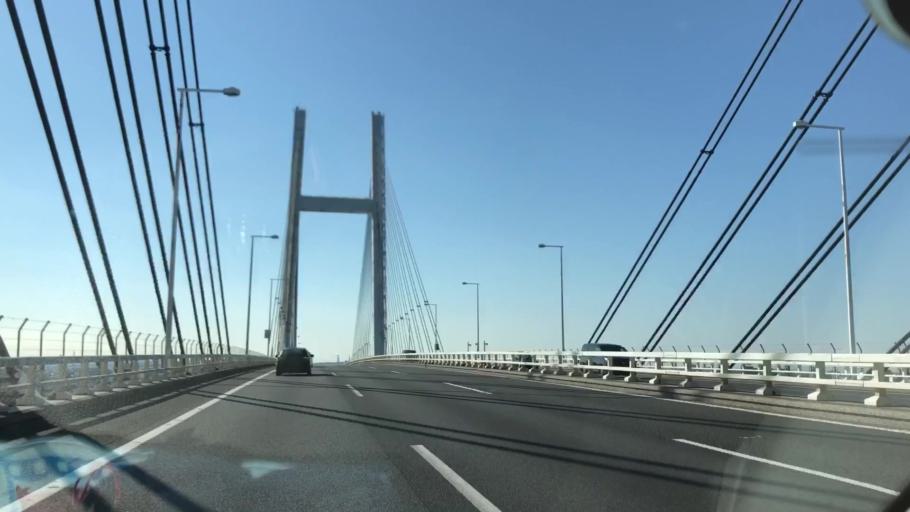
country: JP
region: Kanagawa
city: Yokohama
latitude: 35.4555
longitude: 139.6747
